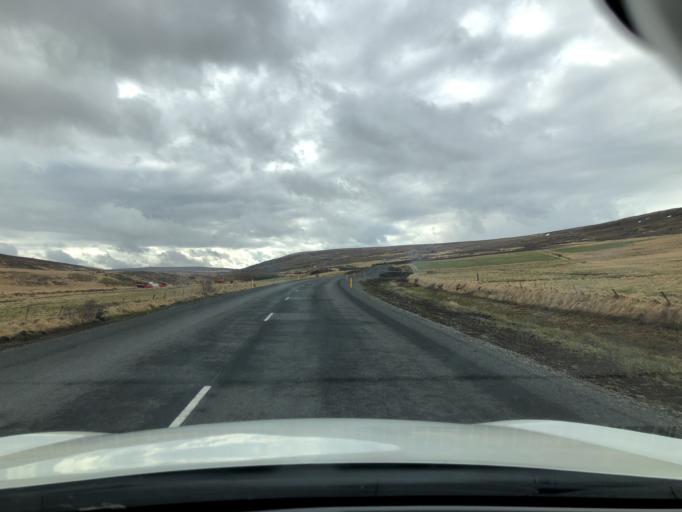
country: IS
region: Northeast
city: Laugar
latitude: 65.6954
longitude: -17.3501
